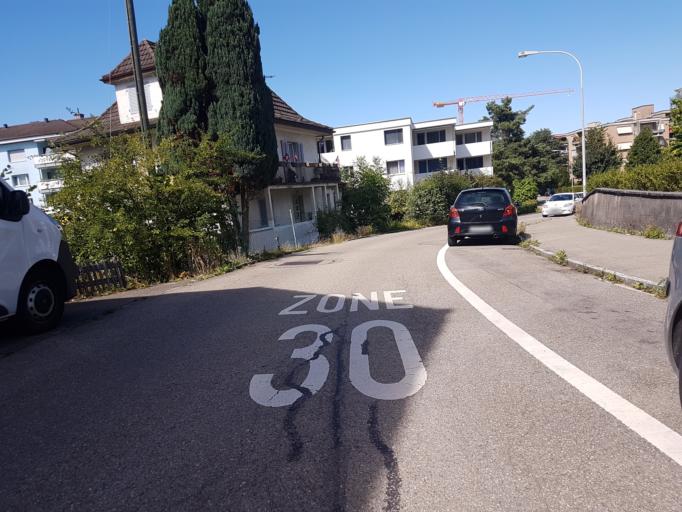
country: CH
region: Zurich
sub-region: Bezirk Pfaeffikon
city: Effretikon
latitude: 47.4242
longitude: 8.6880
